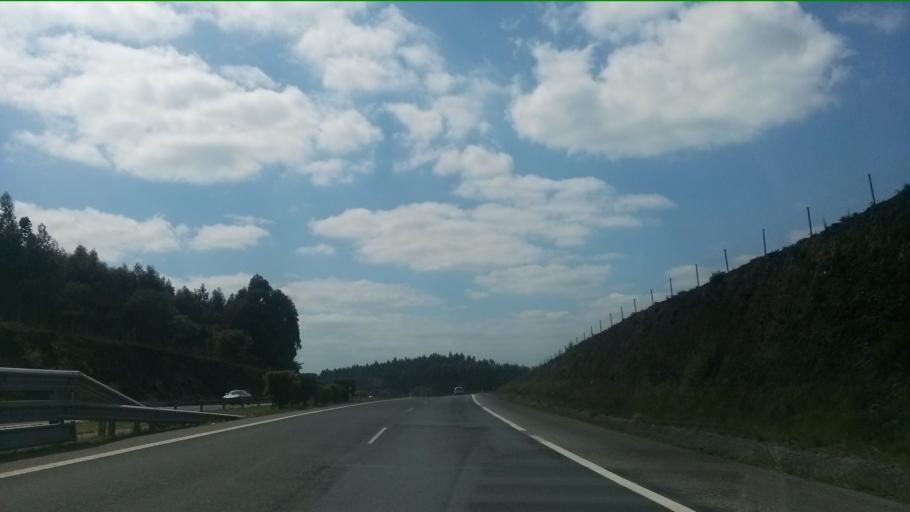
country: ES
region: Galicia
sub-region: Provincia da Coruna
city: Oroso
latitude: 42.9105
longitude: -8.4514
